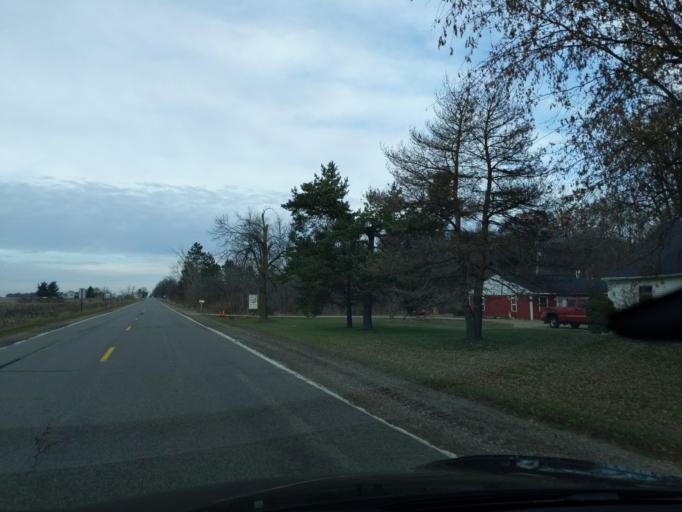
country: US
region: Michigan
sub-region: Ingham County
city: Williamston
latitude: 42.6442
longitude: -84.3638
